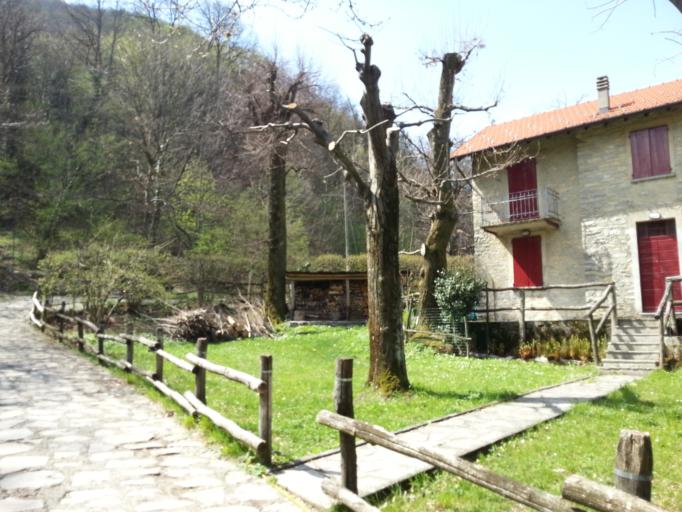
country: IT
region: Lombardy
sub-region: Provincia di Como
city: Torno
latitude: 45.8485
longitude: 9.1248
